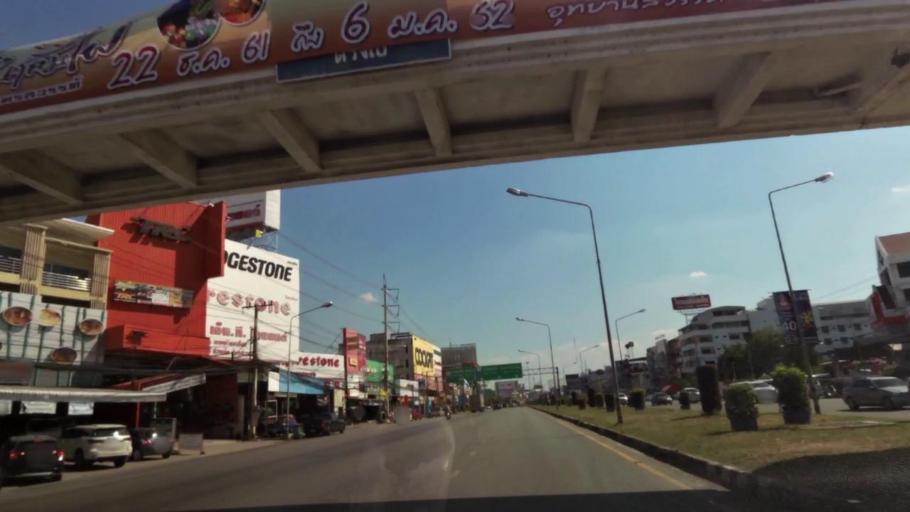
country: TH
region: Nakhon Sawan
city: Nakhon Sawan
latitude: 15.7007
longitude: 100.1179
